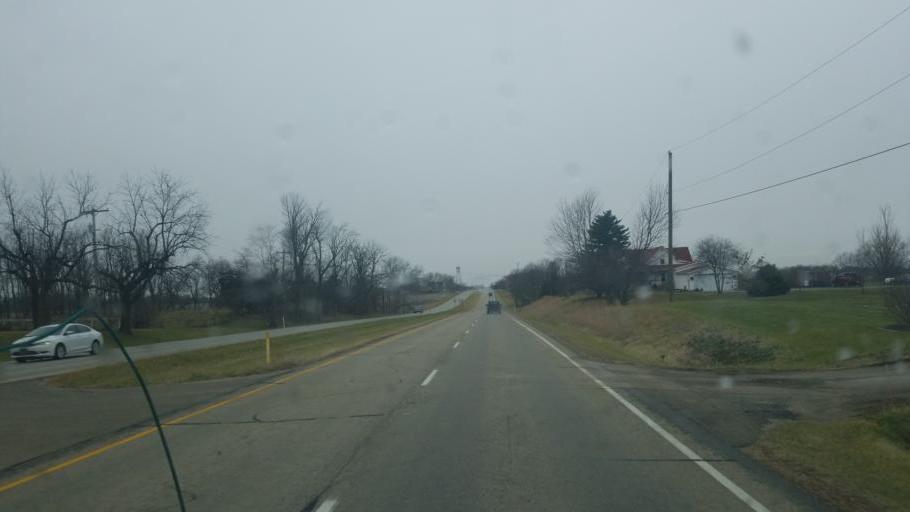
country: US
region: Indiana
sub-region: Hancock County
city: Greenfield
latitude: 39.7902
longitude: -85.6519
